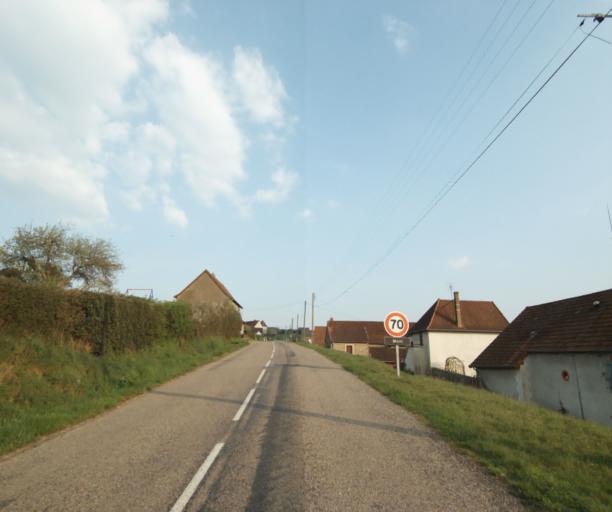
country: FR
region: Bourgogne
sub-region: Departement de Saone-et-Loire
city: Matour
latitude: 46.4192
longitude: 4.4535
